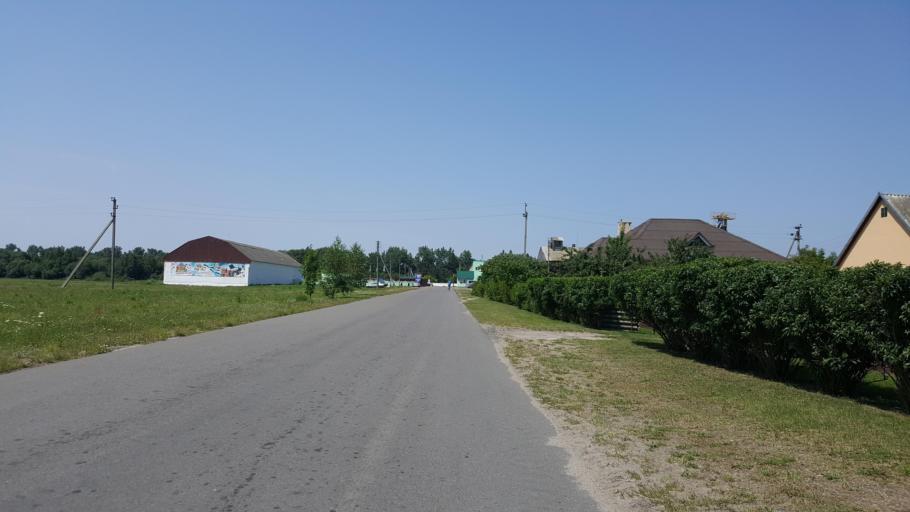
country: BY
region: Brest
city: Zhabinka
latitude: 52.1881
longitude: 23.9960
